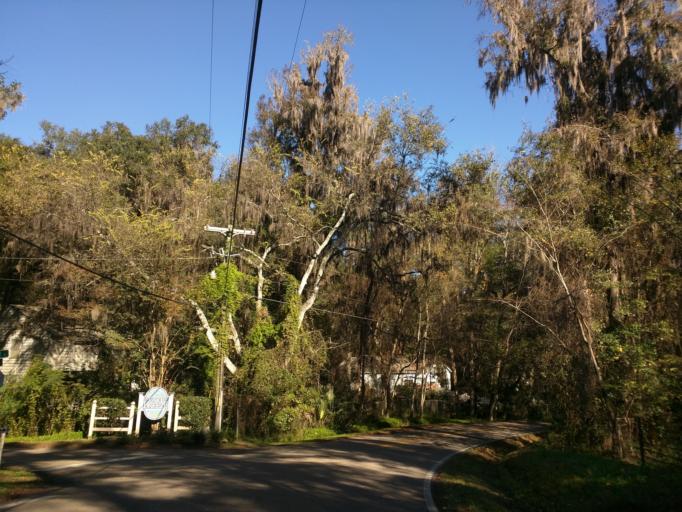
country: US
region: Florida
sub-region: Leon County
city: Tallahassee
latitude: 30.5070
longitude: -84.3213
